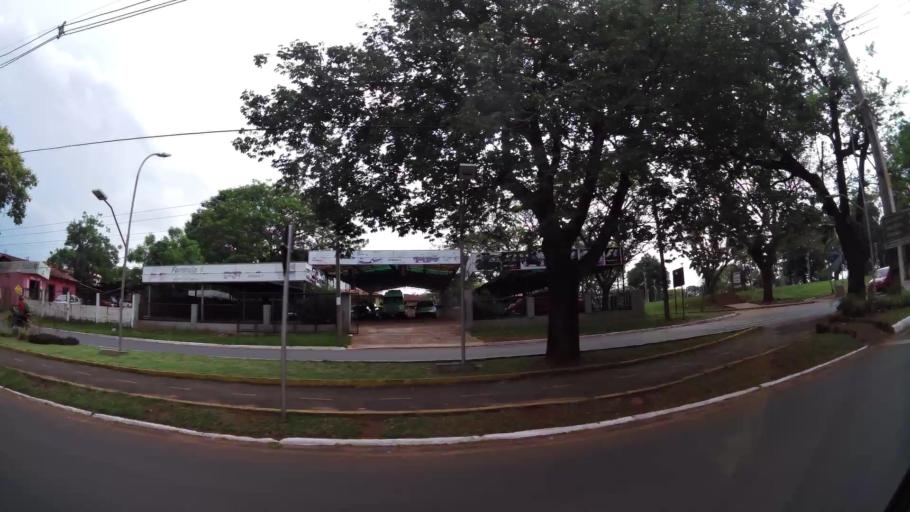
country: PY
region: Alto Parana
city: Ciudad del Este
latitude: -25.5197
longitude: -54.6113
